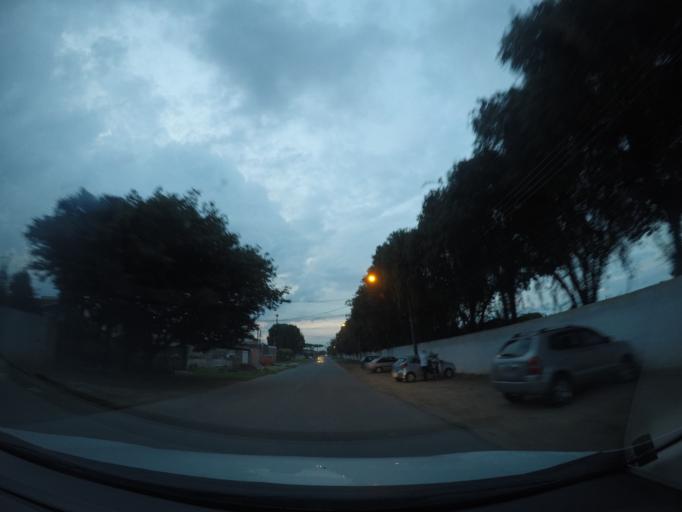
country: BR
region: Parana
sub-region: Sao Jose Dos Pinhais
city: Sao Jose dos Pinhais
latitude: -25.5032
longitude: -49.2284
